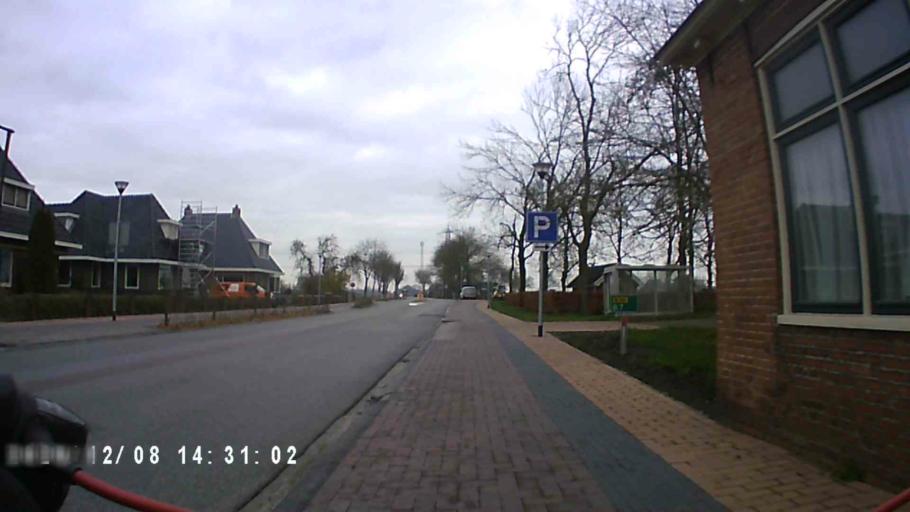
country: NL
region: Groningen
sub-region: Gemeente Winsum
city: Winsum
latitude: 53.2957
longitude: 6.5335
